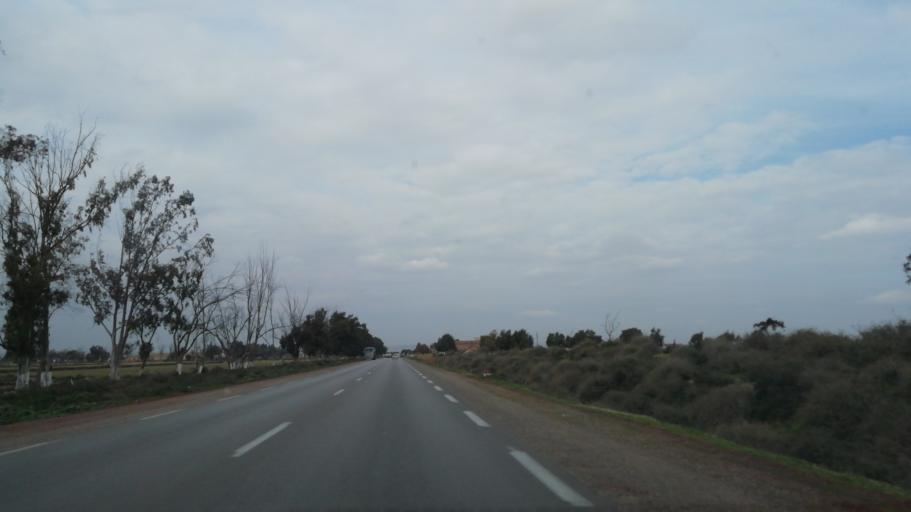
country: DZ
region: Mostaganem
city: Mostaganem
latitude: 35.6802
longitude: 0.0570
